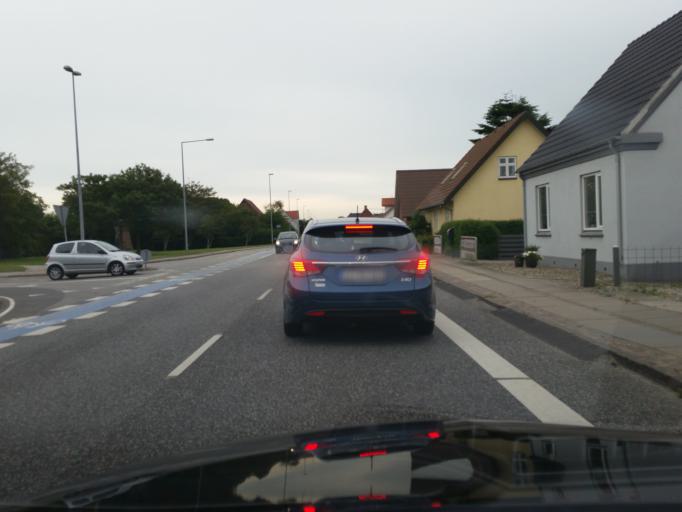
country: DK
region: South Denmark
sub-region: Varde Kommune
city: Oksbol
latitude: 55.7806
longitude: 8.2818
